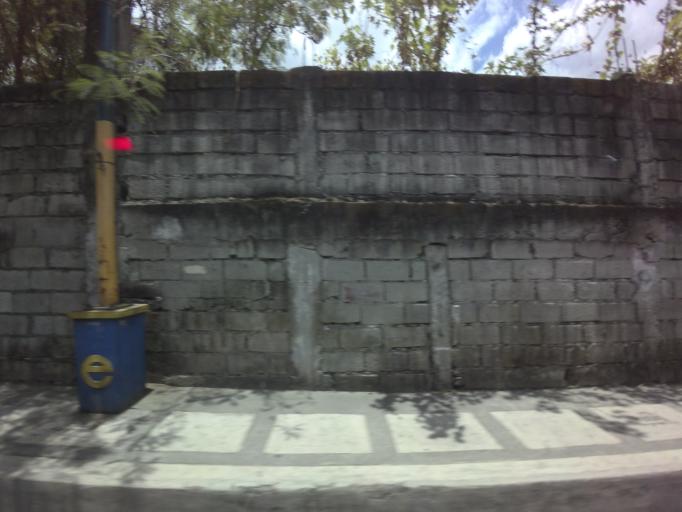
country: PH
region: Metro Manila
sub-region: Marikina
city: Calumpang
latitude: 14.6054
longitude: 121.1043
